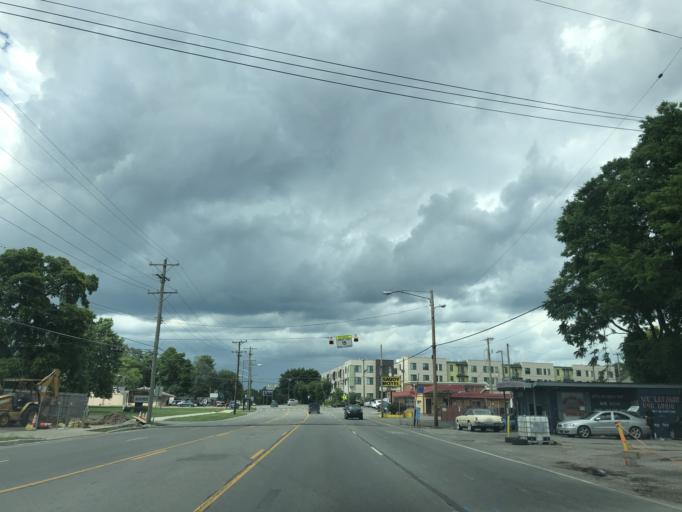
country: US
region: Tennessee
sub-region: Davidson County
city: Nashville
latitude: 36.1989
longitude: -86.7705
